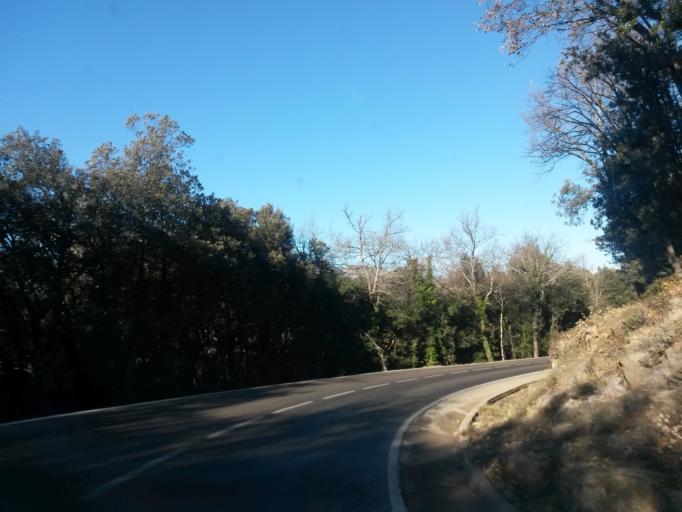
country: ES
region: Catalonia
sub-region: Provincia de Girona
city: Sant Feliu de Pallerols
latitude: 42.0856
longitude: 2.4739
